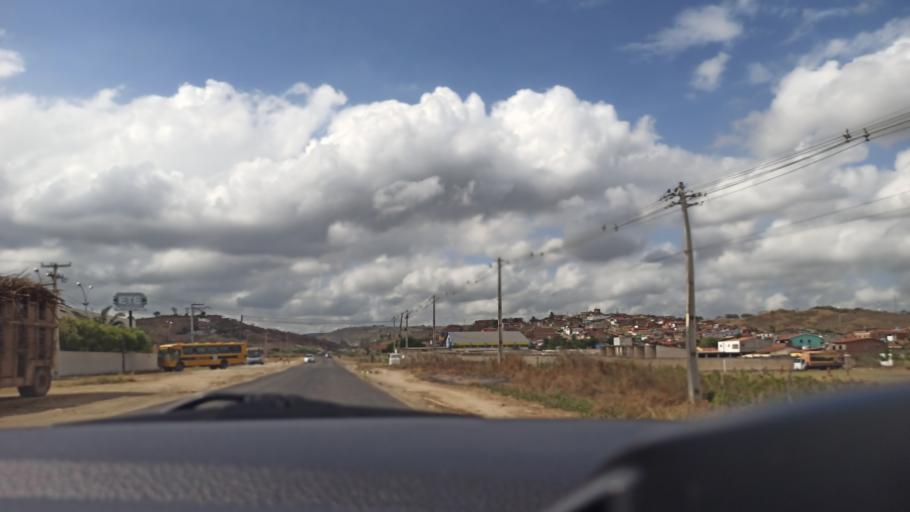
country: BR
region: Pernambuco
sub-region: Timbauba
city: Timbauba
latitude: -7.4984
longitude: -35.2981
